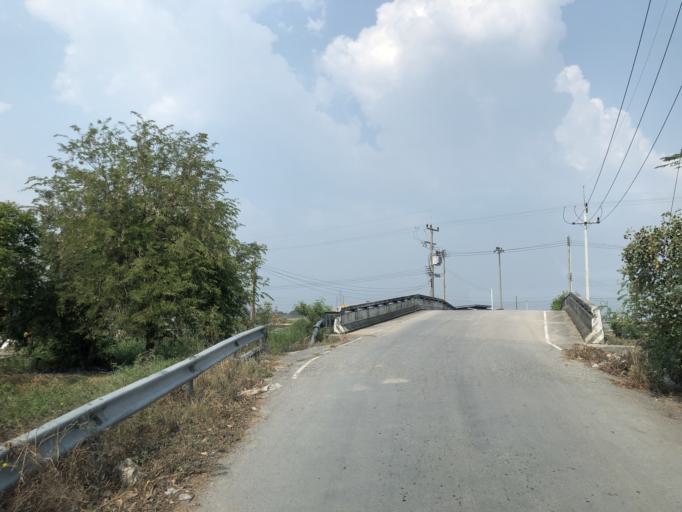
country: TH
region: Samut Prakan
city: Bang Bo
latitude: 13.5381
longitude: 100.8790
